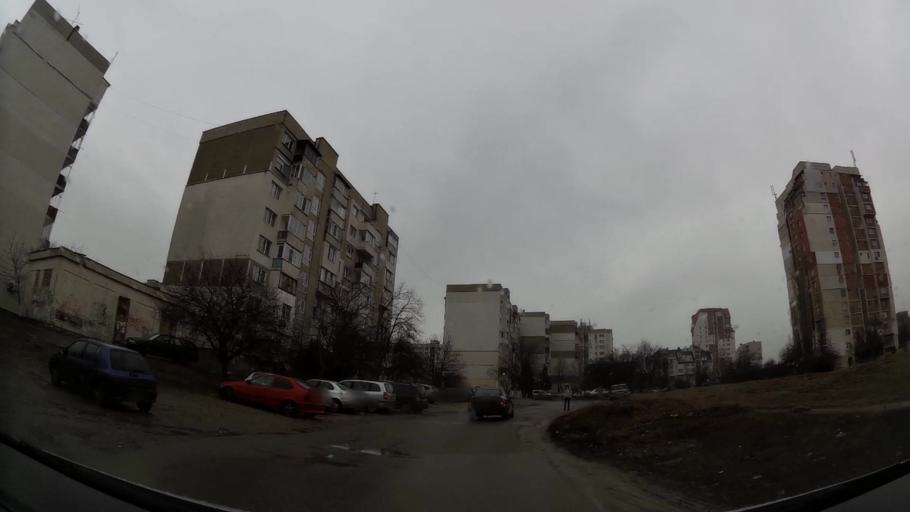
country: BG
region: Sofia-Capital
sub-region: Stolichna Obshtina
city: Sofia
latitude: 42.6293
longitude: 23.3809
